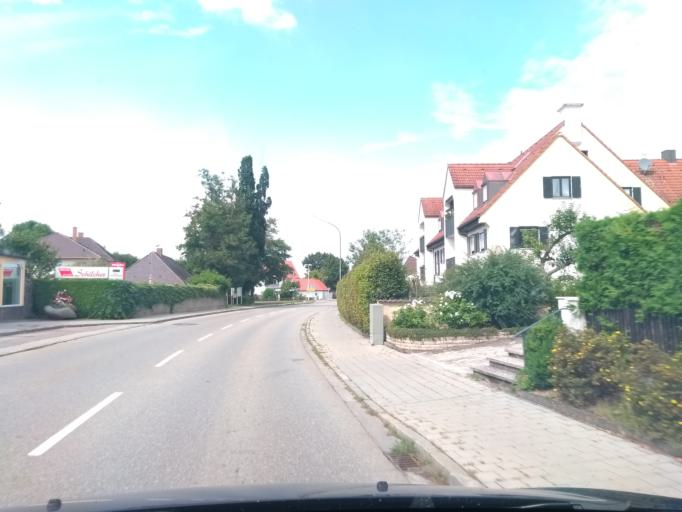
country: DE
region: Bavaria
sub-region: Upper Bavaria
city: Markt Indersdorf
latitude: 48.3547
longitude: 11.3808
